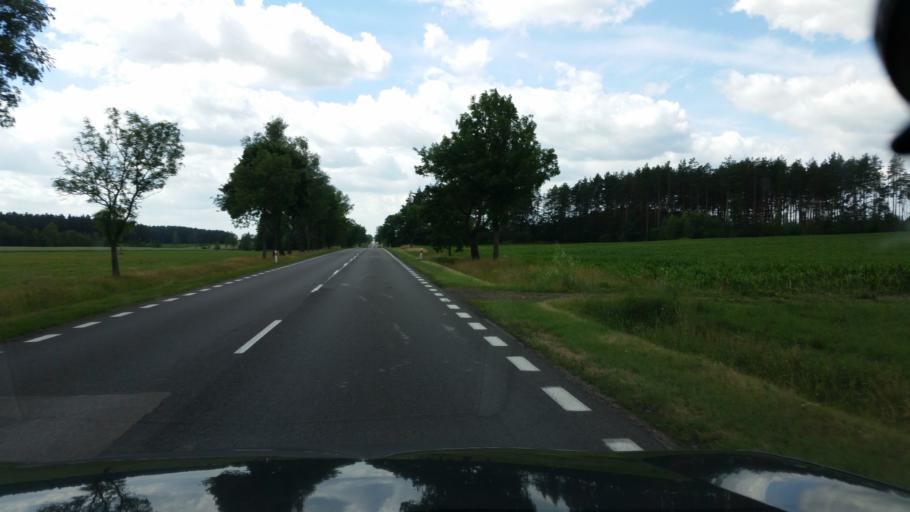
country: PL
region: Podlasie
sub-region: Powiat kolnenski
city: Stawiski
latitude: 53.4727
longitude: 22.2070
